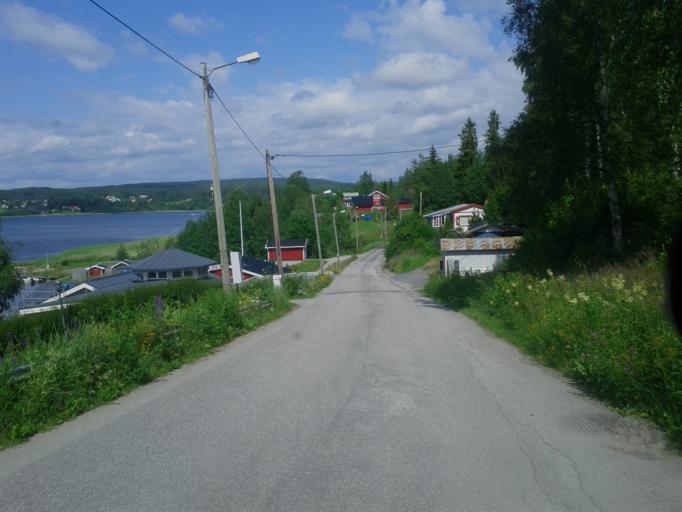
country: SE
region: Vaesternorrland
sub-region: OErnskoeldsviks Kommun
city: Ornskoldsvik
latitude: 63.2576
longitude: 18.8095
